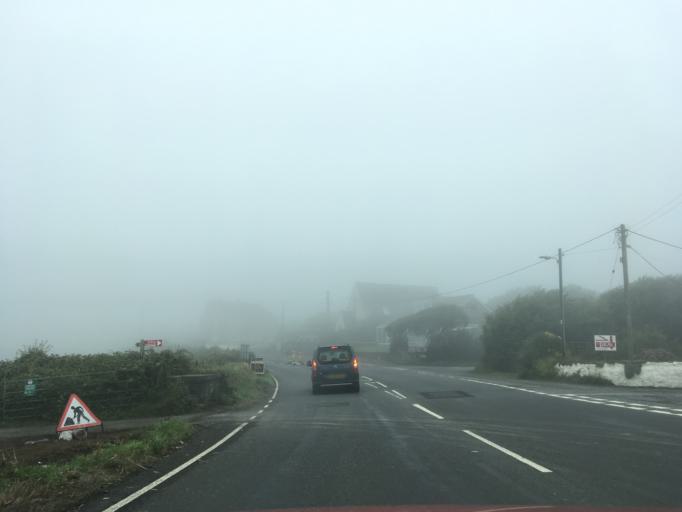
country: GB
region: Wales
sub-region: Pembrokeshire
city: Llanrhian
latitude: 51.8672
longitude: -5.1250
